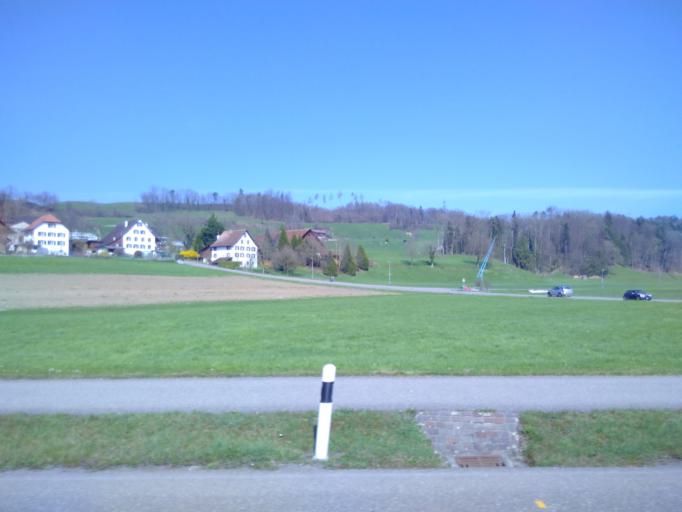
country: CH
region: Zurich
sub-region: Bezirk Hinwil
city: Rueti / Oberdorf
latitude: 47.2325
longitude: 8.8805
